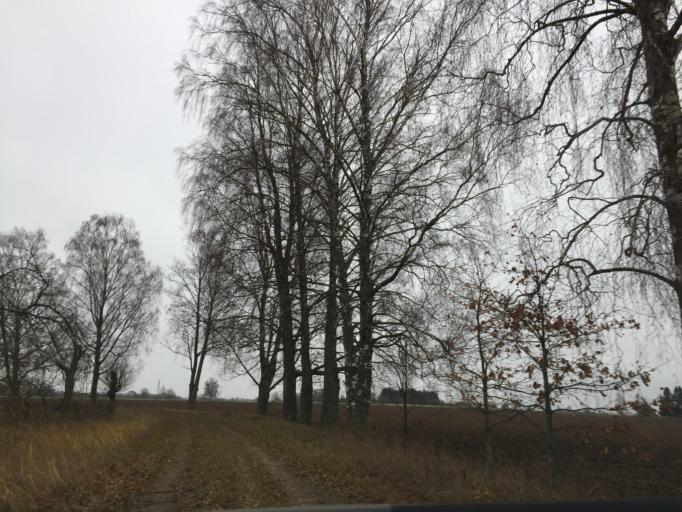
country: LV
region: Limbazu Rajons
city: Limbazi
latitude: 57.4636
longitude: 24.7118
